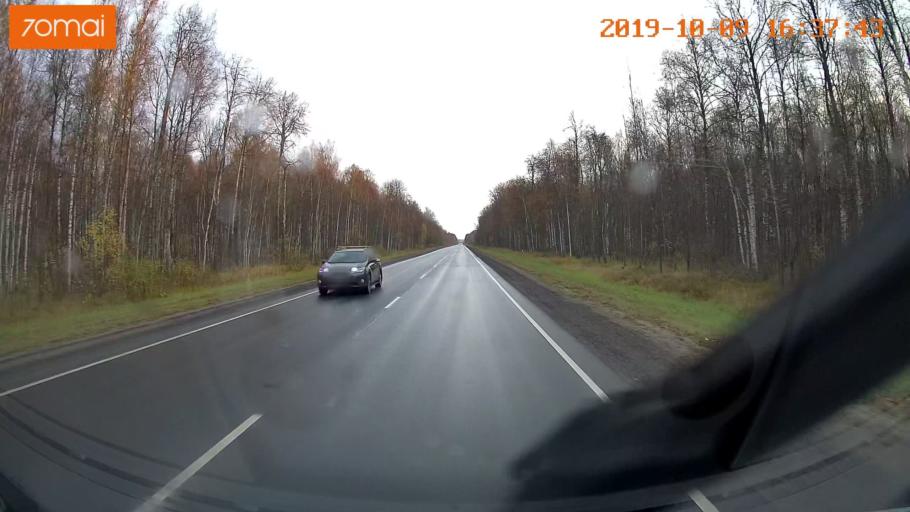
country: RU
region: Kostroma
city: Volgorechensk
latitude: 57.5226
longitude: 41.0282
